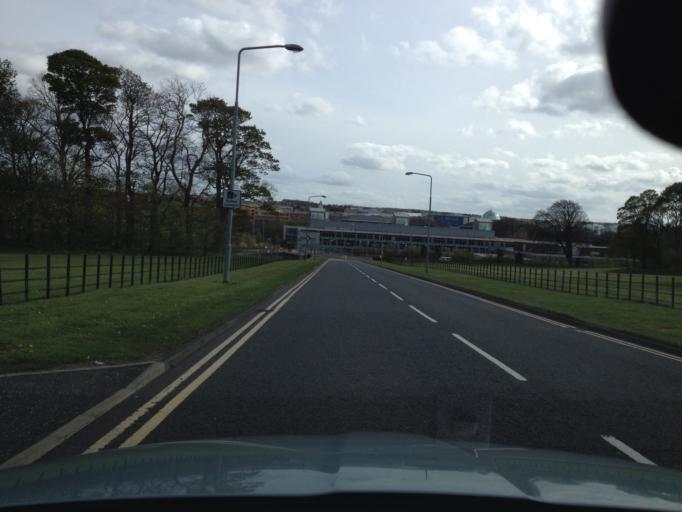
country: GB
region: Scotland
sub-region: West Lothian
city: Livingston
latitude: 55.8900
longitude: -3.5141
